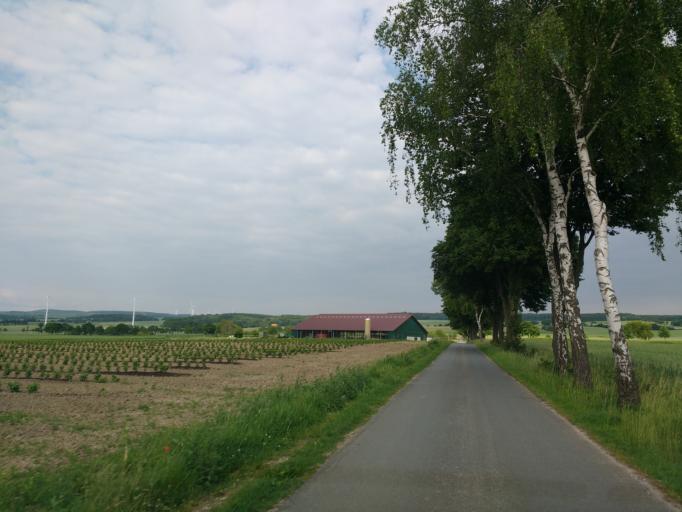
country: DE
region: North Rhine-Westphalia
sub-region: Regierungsbezirk Detmold
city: Schlangen
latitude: 51.7870
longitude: 8.8423
